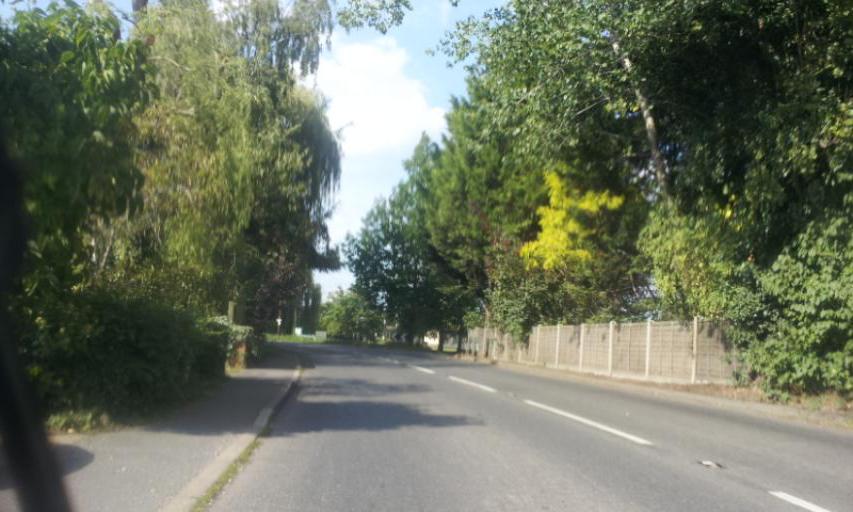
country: GB
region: England
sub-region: Kent
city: Yalding
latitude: 51.1952
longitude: 0.4531
